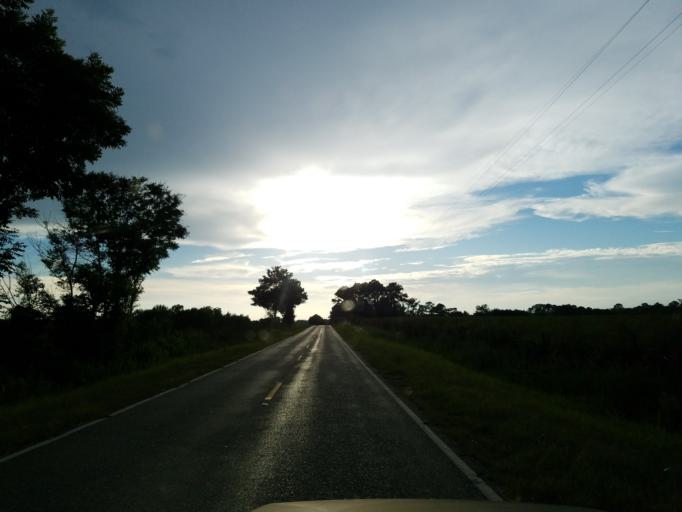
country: US
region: Georgia
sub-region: Tift County
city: Tifton
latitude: 31.5514
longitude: -83.5566
